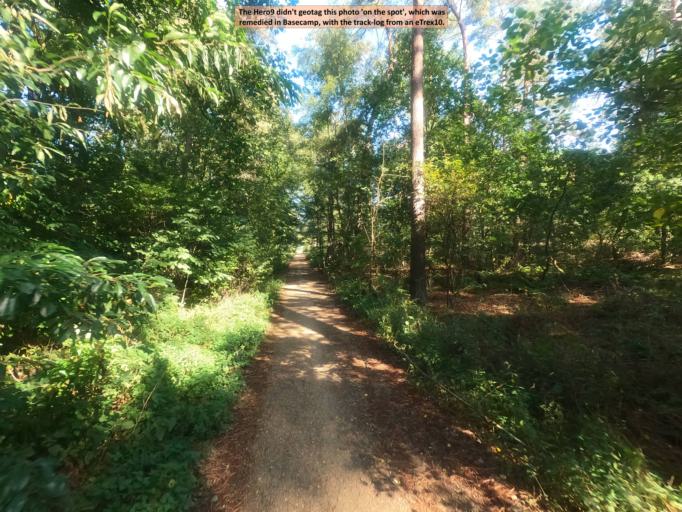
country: BE
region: Flanders
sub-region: Provincie Antwerpen
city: Herentals
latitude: 51.2028
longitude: 4.8410
